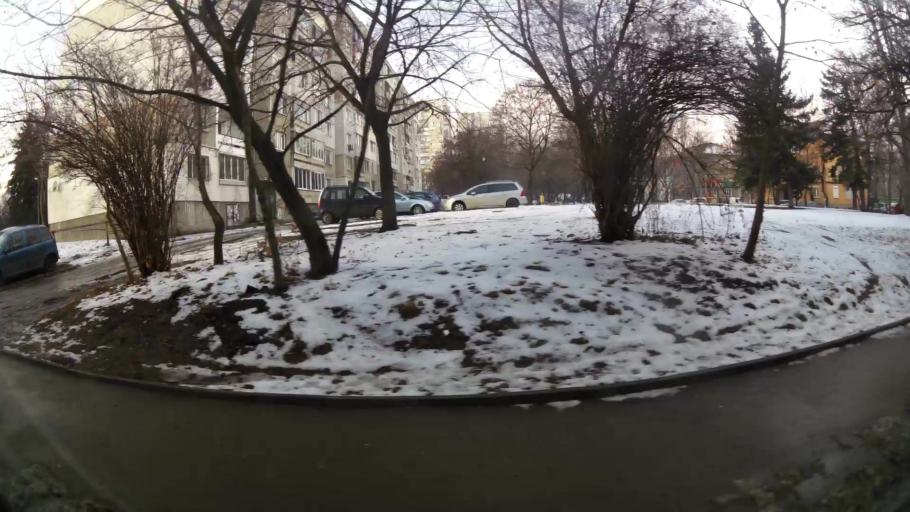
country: BG
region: Sofia-Capital
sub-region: Stolichna Obshtina
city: Sofia
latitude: 42.6993
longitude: 23.2801
